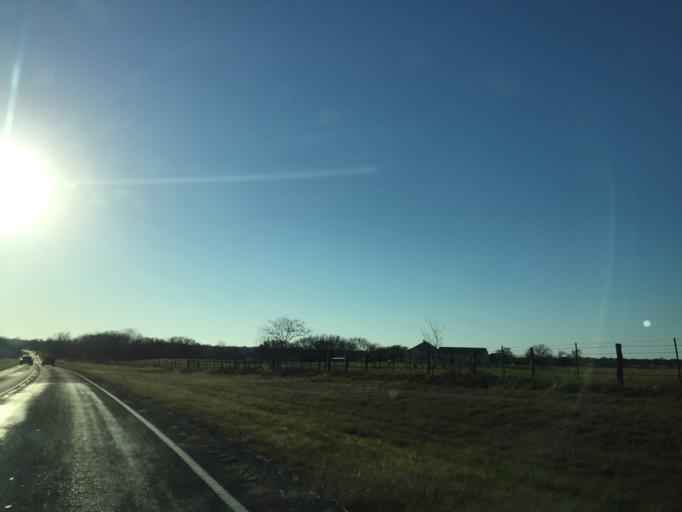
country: US
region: Texas
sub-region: Bastrop County
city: Elgin
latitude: 30.3590
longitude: -97.3472
